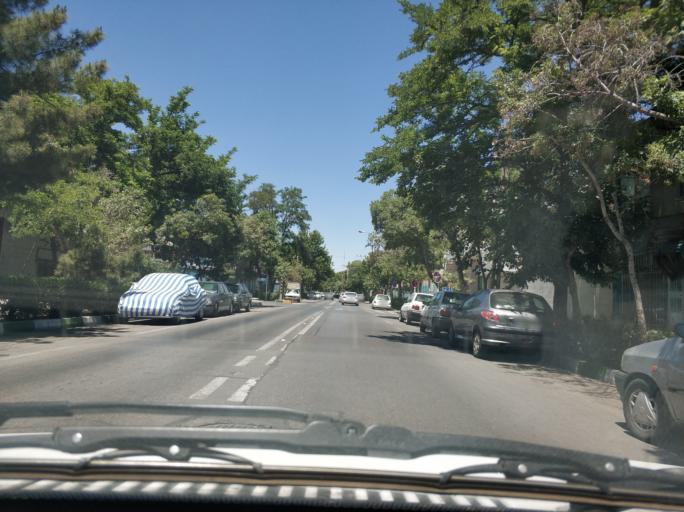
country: IR
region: Razavi Khorasan
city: Mashhad
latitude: 36.2762
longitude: 59.5907
